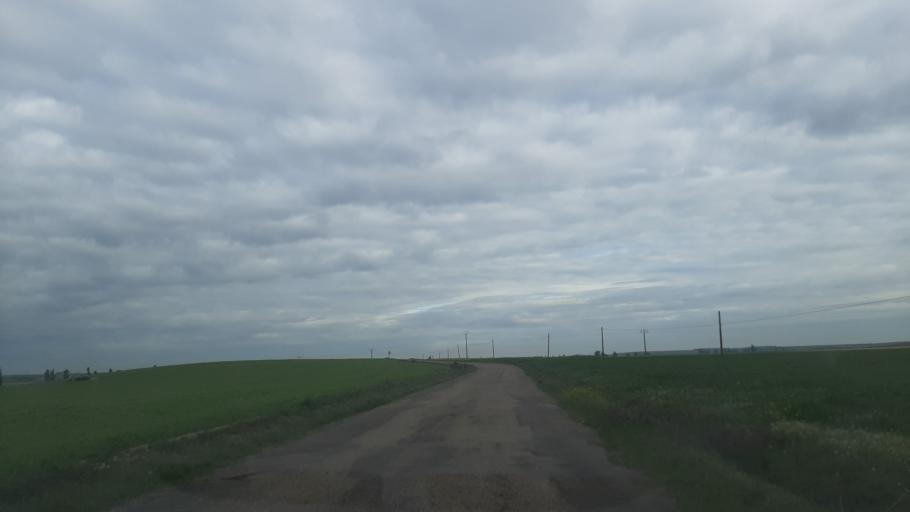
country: ES
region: Castille and Leon
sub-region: Provincia de Salamanca
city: Villaflores
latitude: 41.0741
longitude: -5.2132
